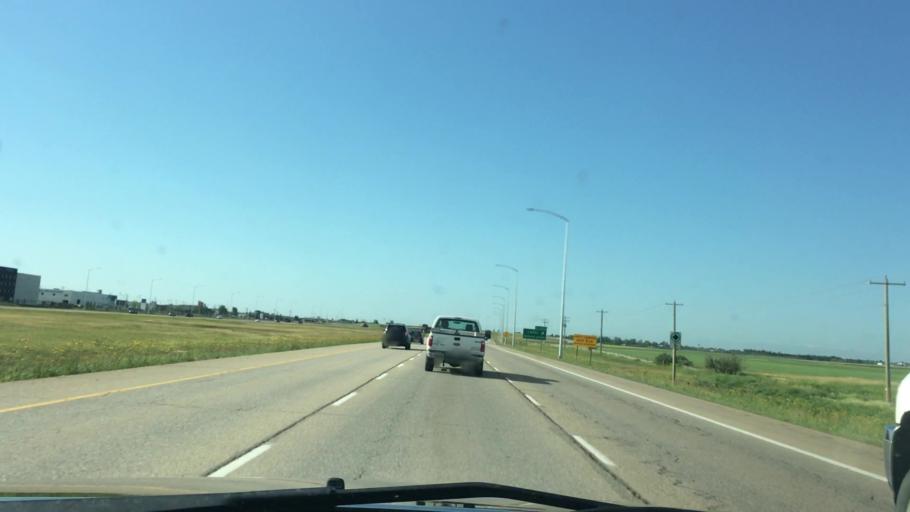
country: CA
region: Alberta
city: Leduc
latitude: 53.2954
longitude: -113.5499
